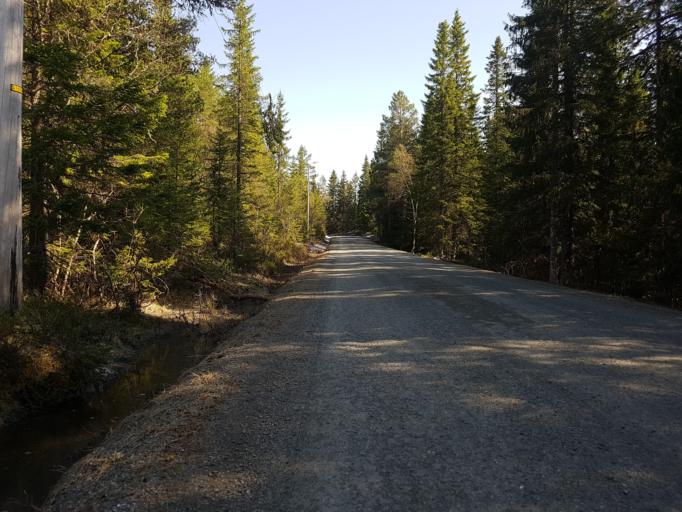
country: NO
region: Sor-Trondelag
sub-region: Trondheim
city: Trondheim
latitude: 63.4265
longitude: 10.2932
